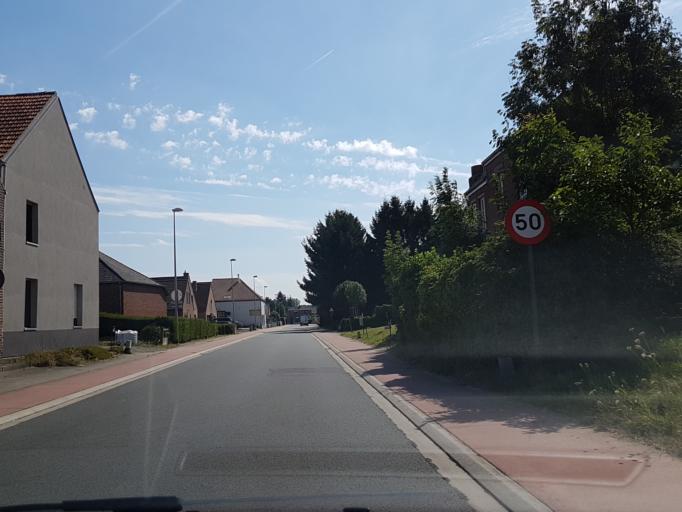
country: BE
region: Flanders
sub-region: Provincie Vlaams-Brabant
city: Herent
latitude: 50.9245
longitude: 4.6306
